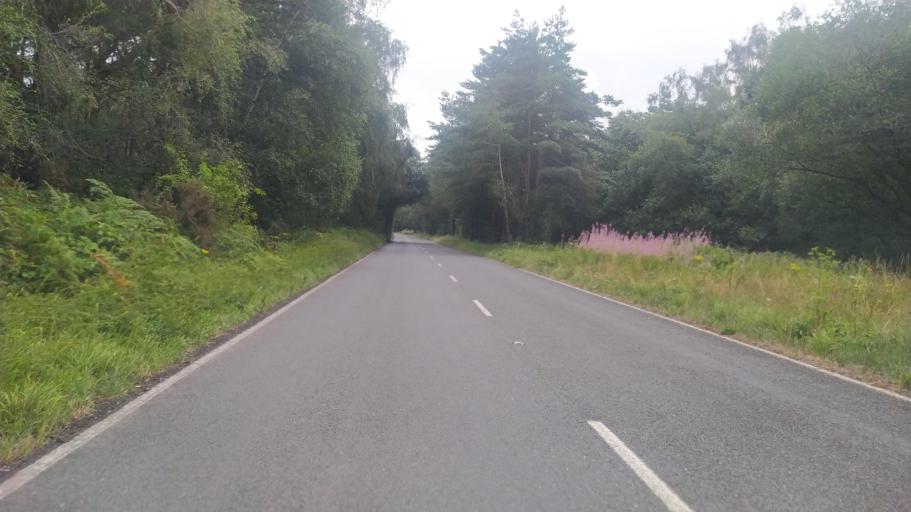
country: GB
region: England
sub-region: West Sussex
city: Milland
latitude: 51.0462
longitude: -0.8376
